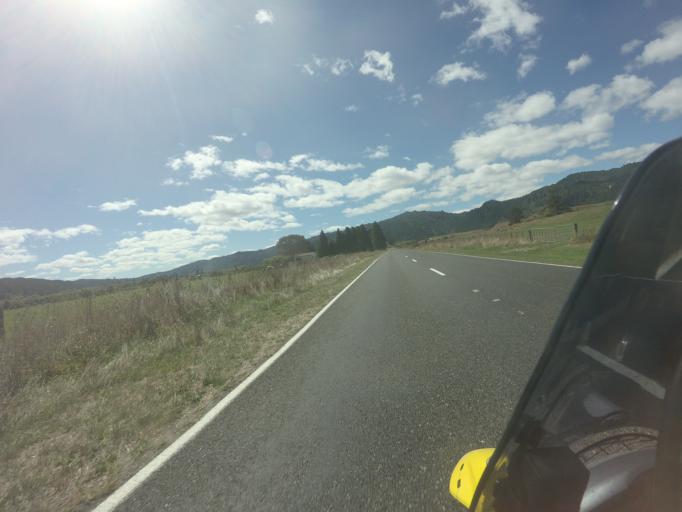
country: NZ
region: Bay of Plenty
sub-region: Kawerau District
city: Kawerau
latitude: -38.2378
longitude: 176.8319
